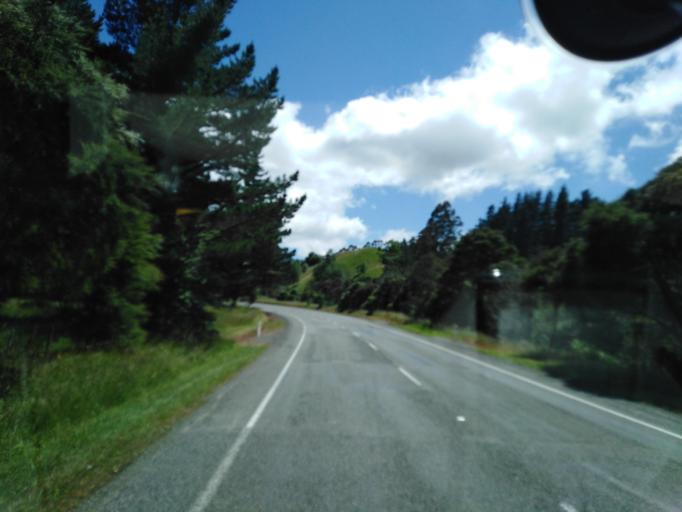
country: NZ
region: Nelson
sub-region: Nelson City
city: Nelson
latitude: -41.2212
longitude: 173.3977
